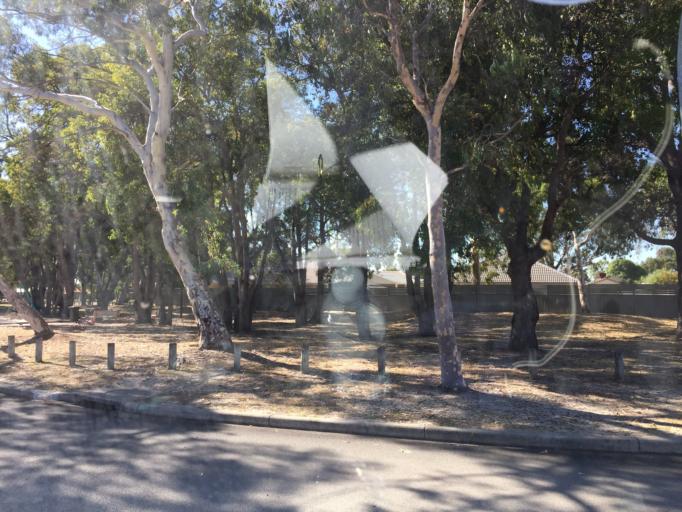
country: AU
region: Western Australia
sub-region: Swan
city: Stratton
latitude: -31.8651
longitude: 116.0425
